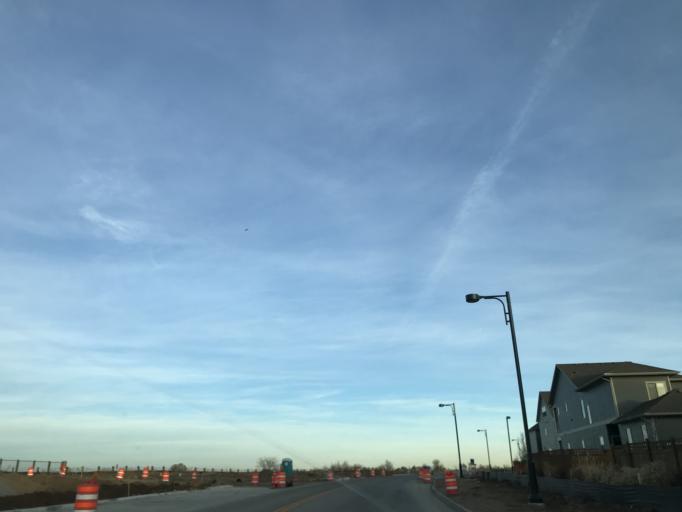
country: US
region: Colorado
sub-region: Adams County
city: Aurora
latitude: 39.7576
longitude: -104.8574
